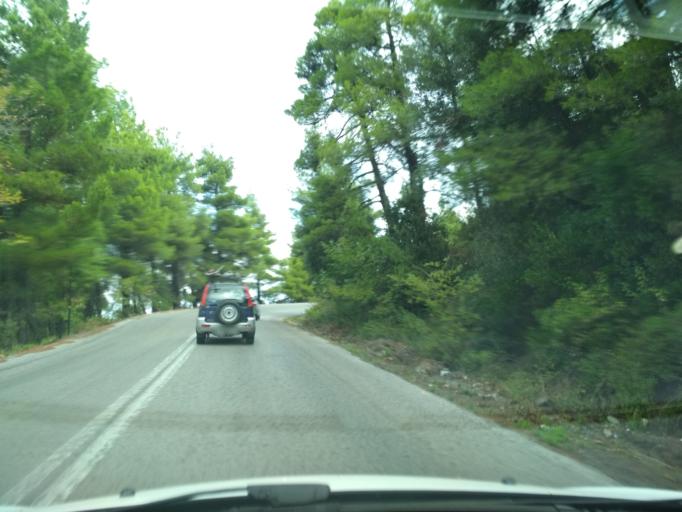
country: GR
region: Central Greece
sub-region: Nomos Evvoias
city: Politika
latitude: 38.6713
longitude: 23.5572
